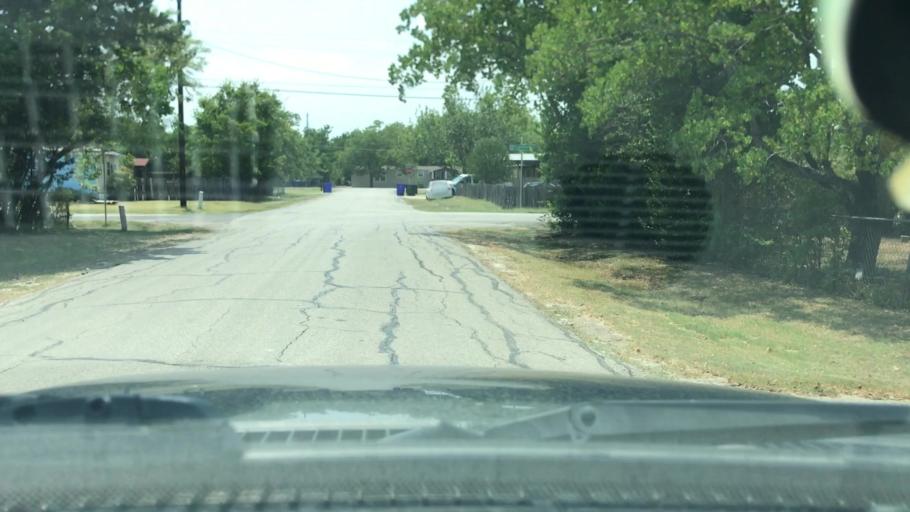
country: US
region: Texas
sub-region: Williamson County
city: Cedar Park
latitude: 30.5352
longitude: -97.8392
